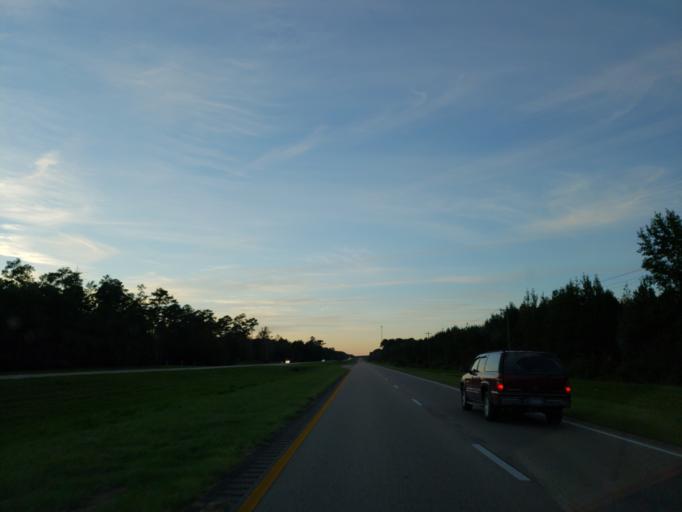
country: US
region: Mississippi
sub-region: Wayne County
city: Belmont
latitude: 31.6057
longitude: -88.5625
